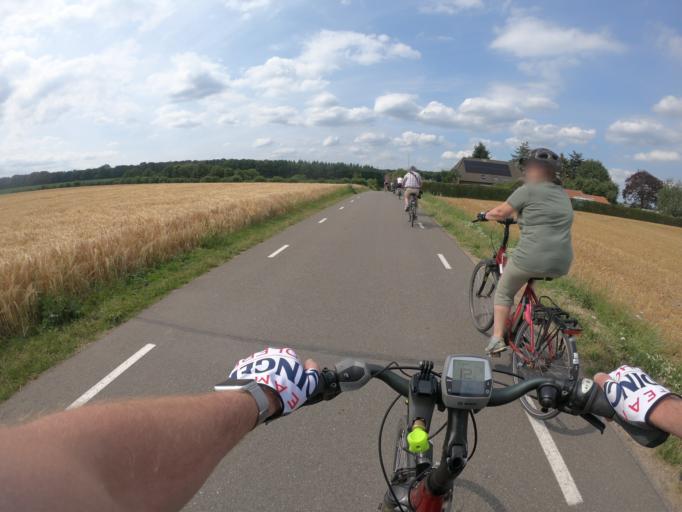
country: NL
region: Gelderland
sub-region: Gemeente Groesbeek
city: Bredeweg
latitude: 51.7657
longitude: 5.9314
